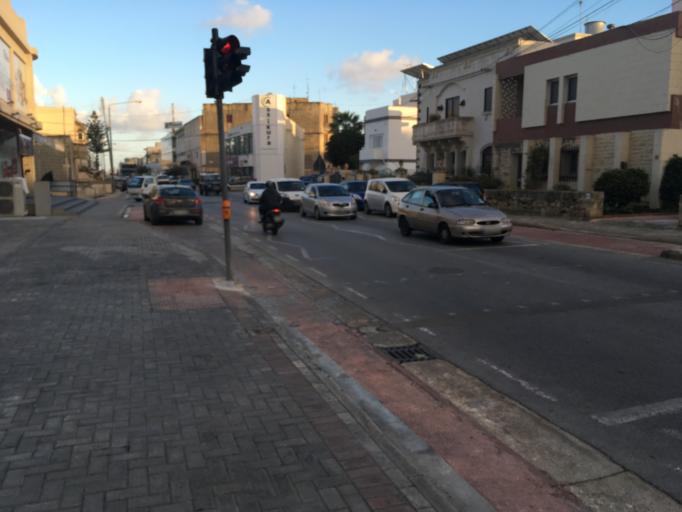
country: MT
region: Saint Venera
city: Santa Venera
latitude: 35.8930
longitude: 14.4768
